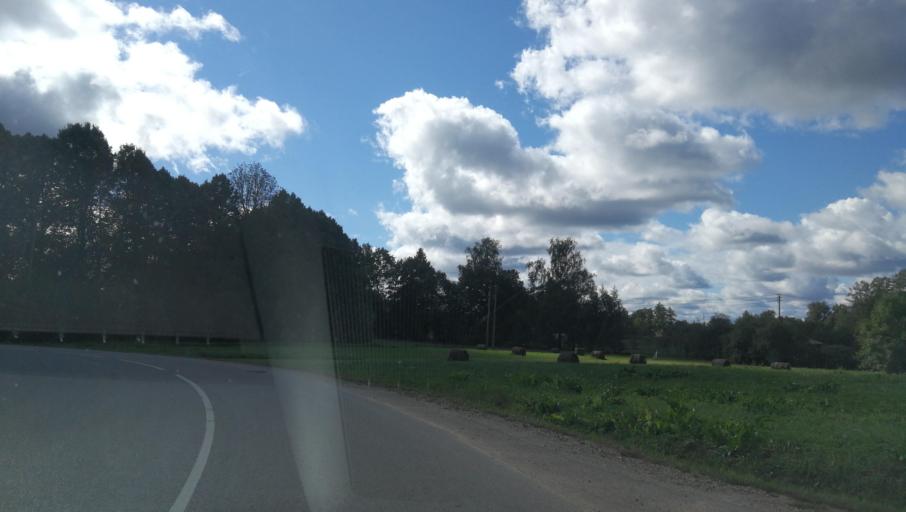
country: LV
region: Cesu Rajons
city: Cesis
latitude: 57.2971
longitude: 25.2333
